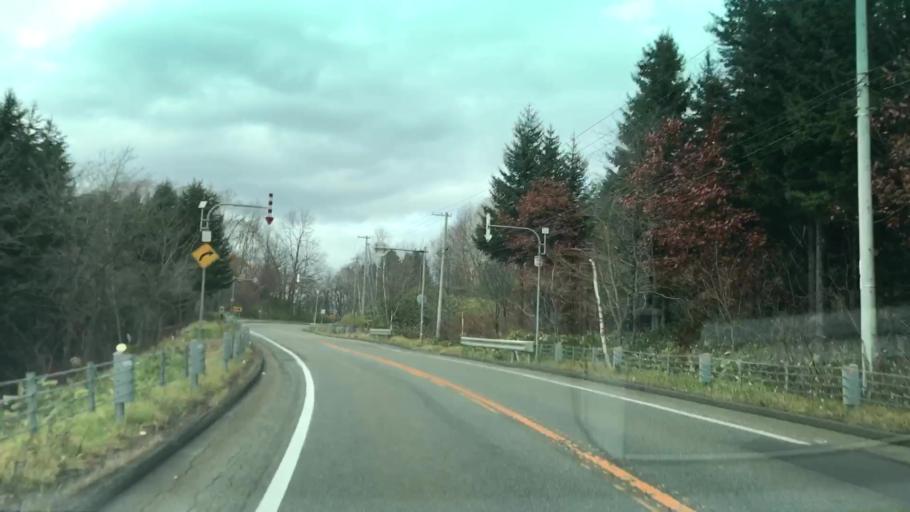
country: JP
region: Hokkaido
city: Shimo-furano
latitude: 42.8898
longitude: 142.4364
